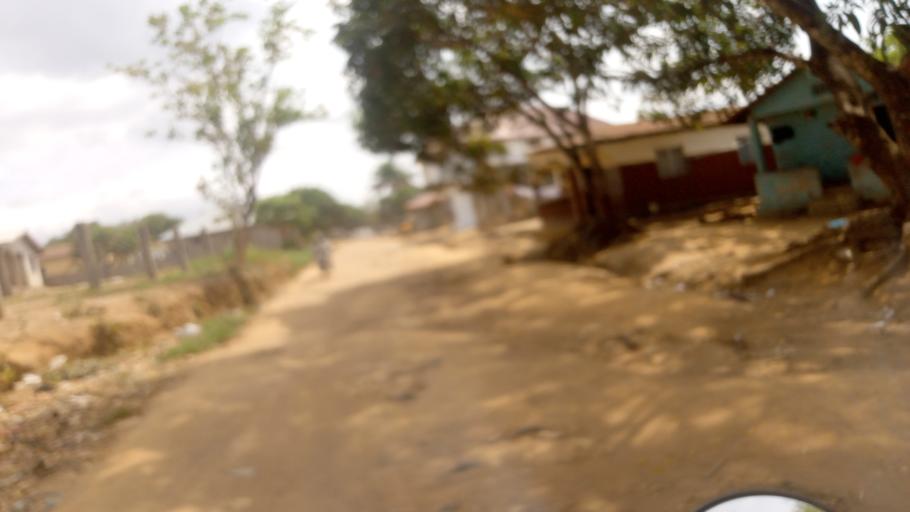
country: SL
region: Western Area
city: Waterloo
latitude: 8.3212
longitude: -13.0636
